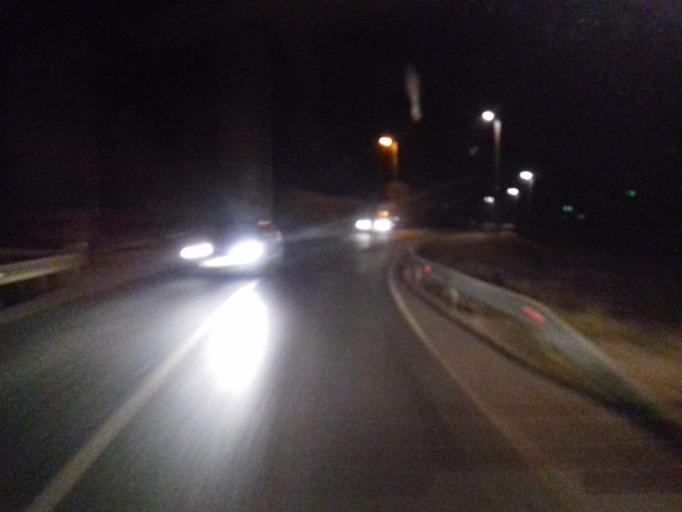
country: BA
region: Federation of Bosnia and Herzegovina
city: Hadzici
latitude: 43.8715
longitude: 18.2072
